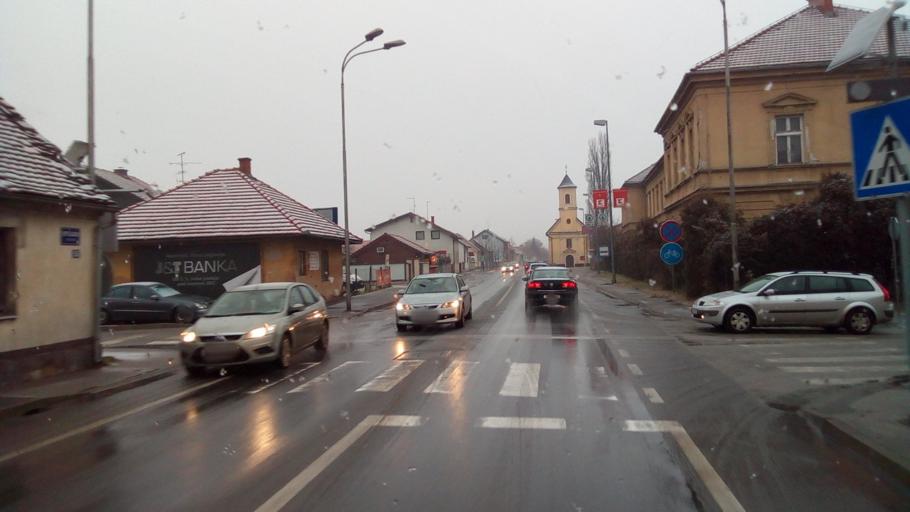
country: HR
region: Varazdinska
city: Varazdin
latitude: 46.3157
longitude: 16.3233
